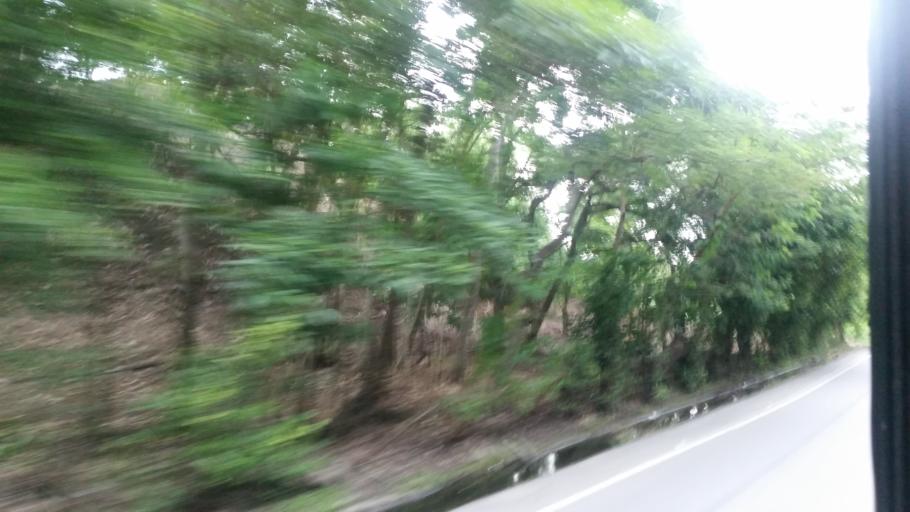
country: CO
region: Magdalena
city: Santa Marta
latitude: 11.2778
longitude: -73.8687
